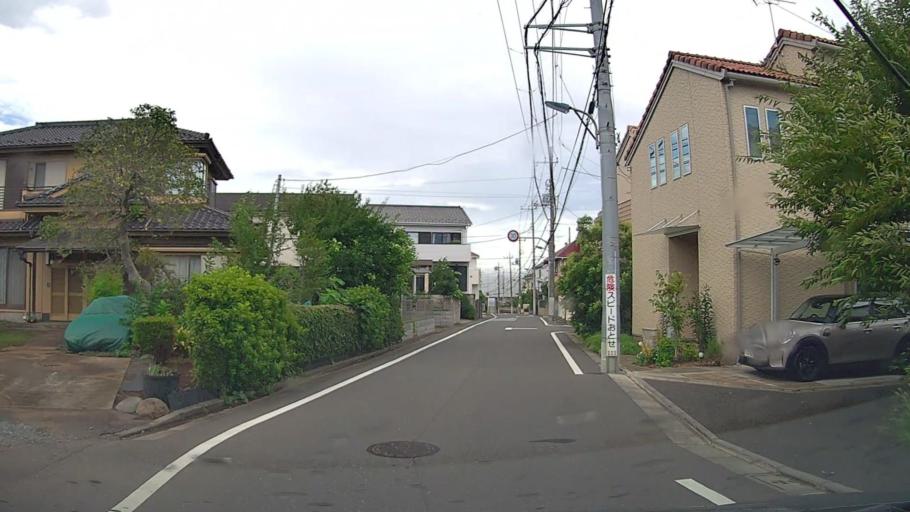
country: JP
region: Saitama
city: Asaka
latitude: 35.7621
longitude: 139.5864
